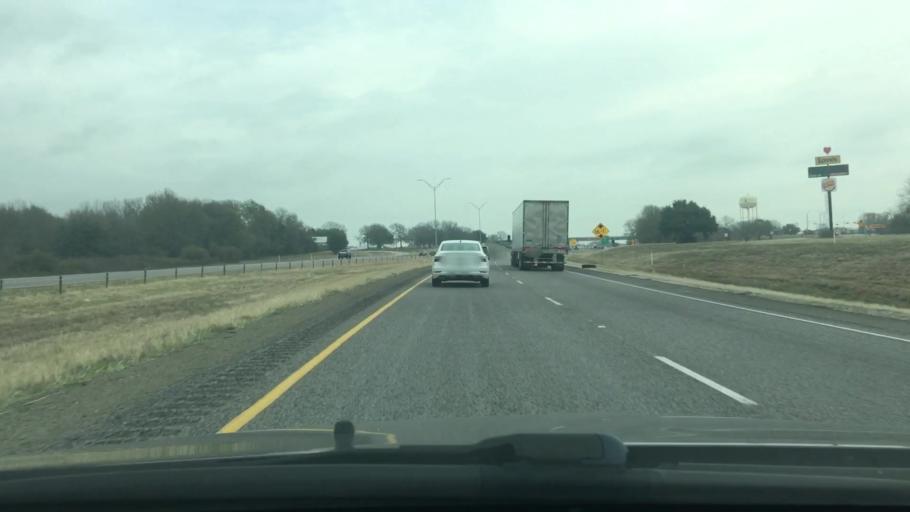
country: US
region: Texas
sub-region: Freestone County
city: Fairfield
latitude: 31.7316
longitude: -96.1825
